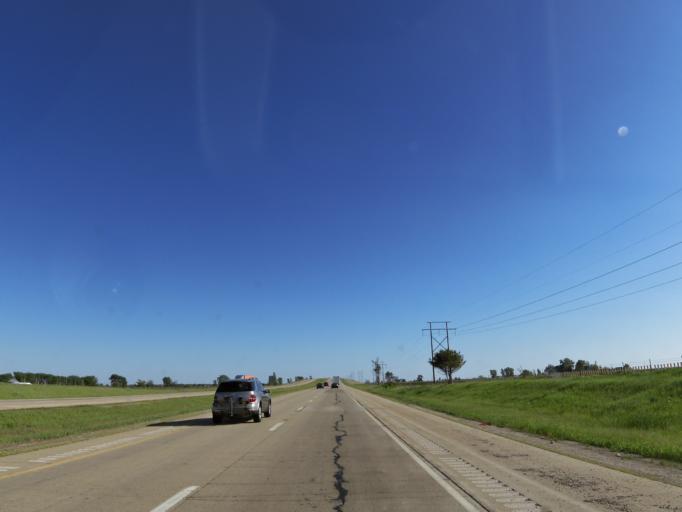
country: US
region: Illinois
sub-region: Marshall County
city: Wenona
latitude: 41.0184
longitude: -89.0566
